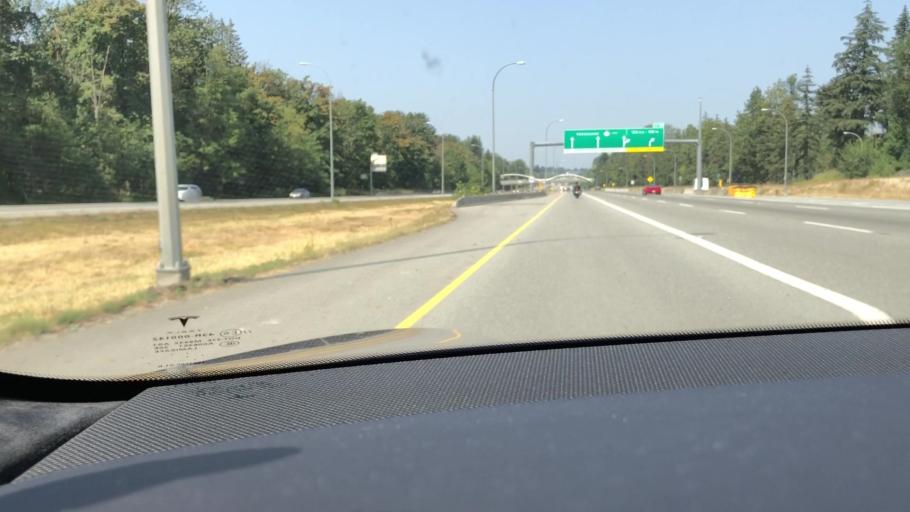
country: CA
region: British Columbia
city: Pitt Meadows
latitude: 49.1851
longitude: -122.7485
